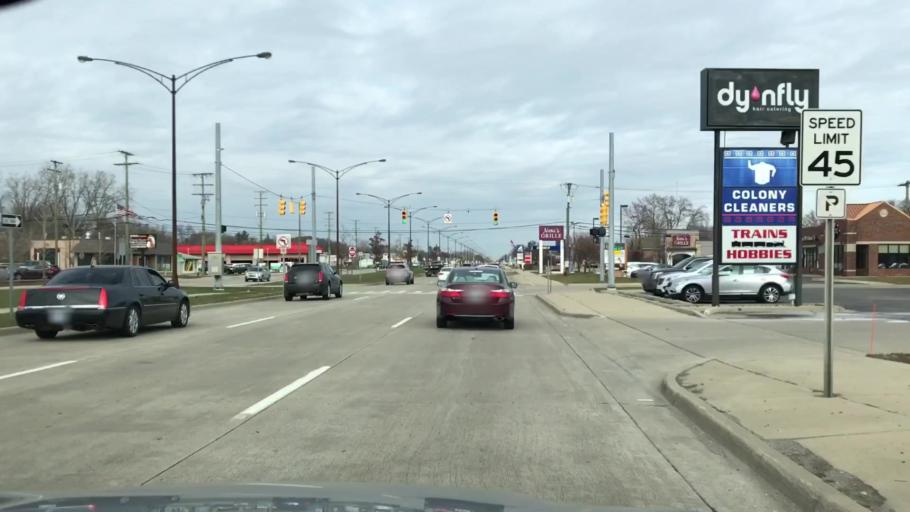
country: US
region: Michigan
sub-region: Oakland County
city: Clawson
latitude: 42.5675
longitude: -83.1273
